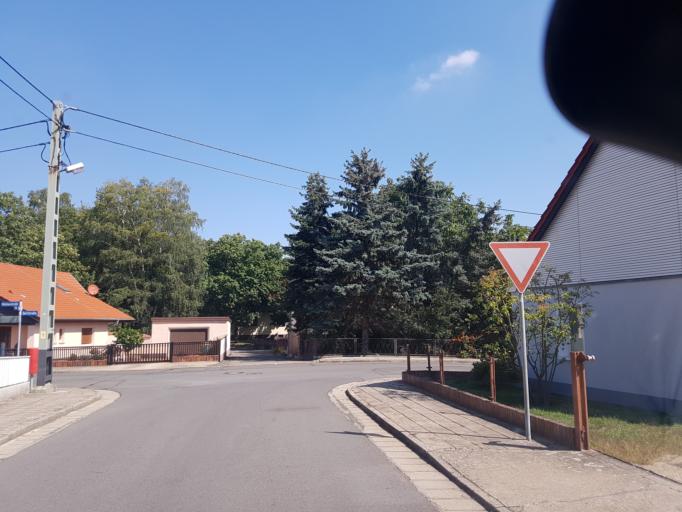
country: DE
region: Brandenburg
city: Elsterwerda
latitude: 51.4949
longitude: 13.5043
